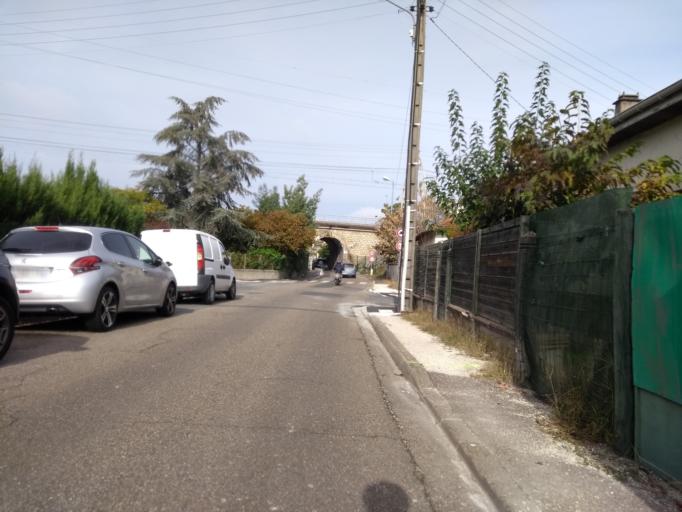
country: FR
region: Aquitaine
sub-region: Departement de la Gironde
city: Talence
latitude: 44.8091
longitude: -0.6176
